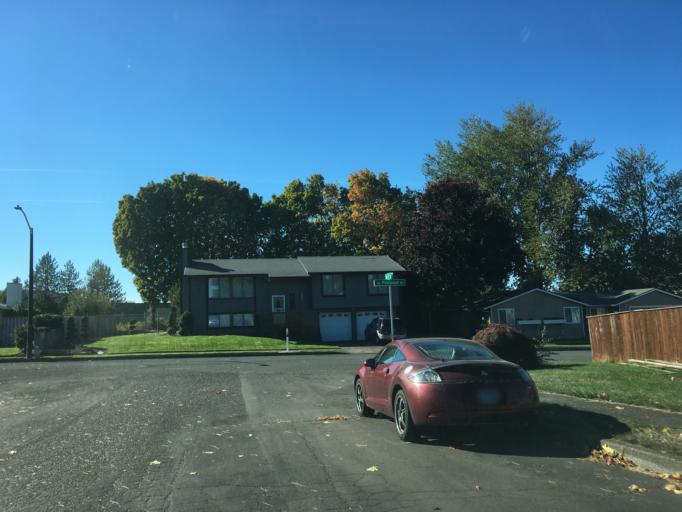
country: US
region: Oregon
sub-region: Multnomah County
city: Gresham
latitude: 45.4955
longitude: -122.4026
